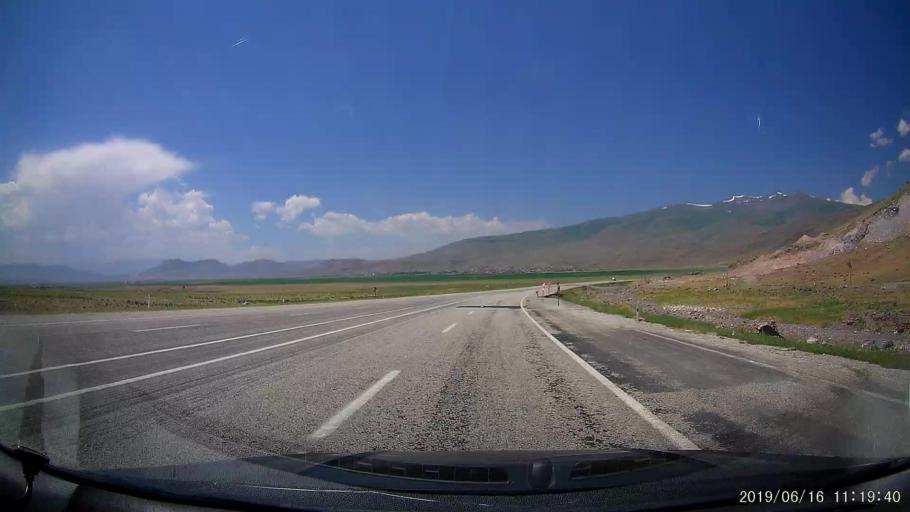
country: TR
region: Agri
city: Dogubayazit
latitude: 39.6964
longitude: 44.1094
